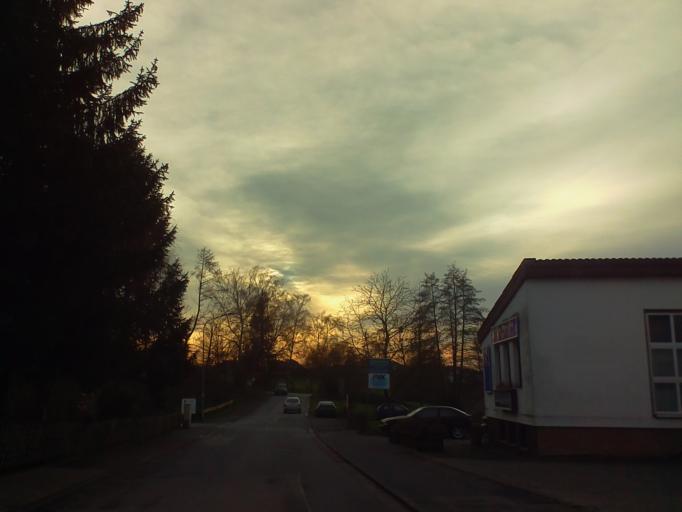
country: DE
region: Hesse
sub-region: Regierungsbezirk Darmstadt
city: Furth
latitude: 49.6559
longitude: 8.7990
